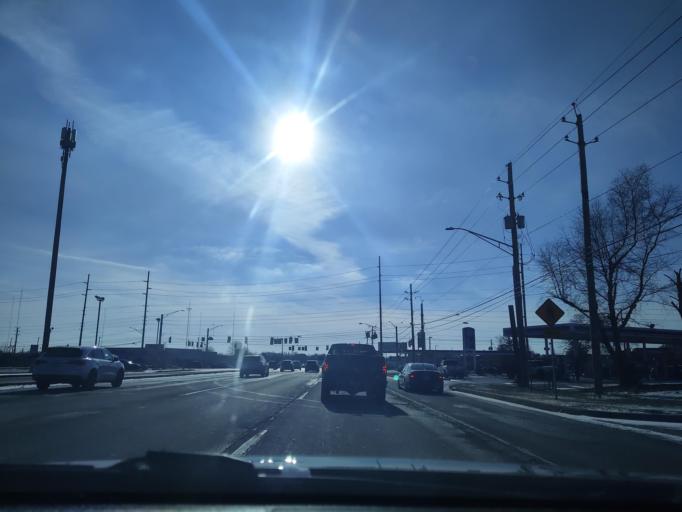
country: US
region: Indiana
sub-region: Boone County
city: Zionsville
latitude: 39.9126
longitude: -86.2232
